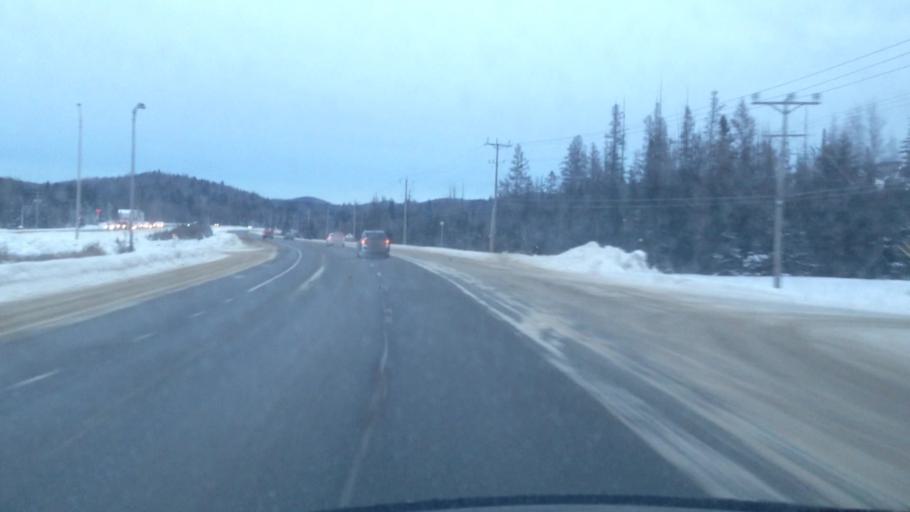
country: CA
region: Quebec
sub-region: Laurentides
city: Mont-Tremblant
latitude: 46.1119
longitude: -74.5294
